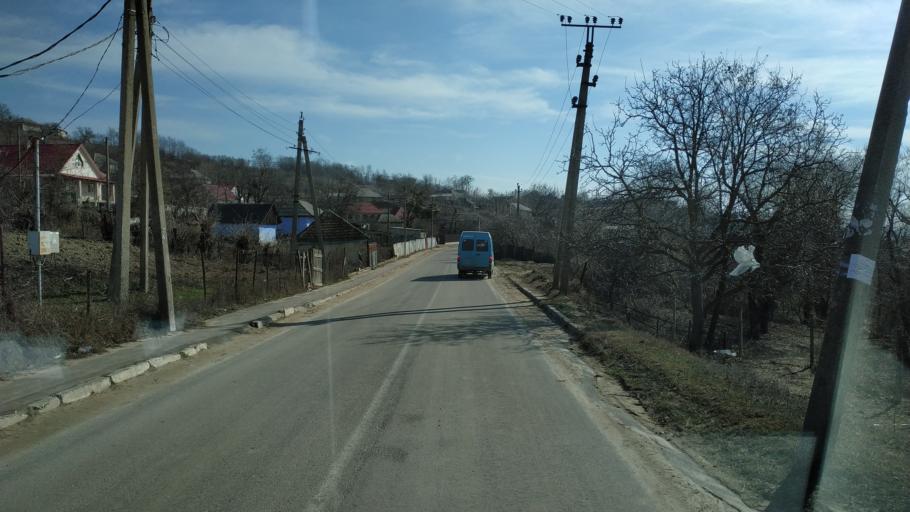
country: MD
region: Nisporeni
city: Nisporeni
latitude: 47.2238
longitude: 28.0463
